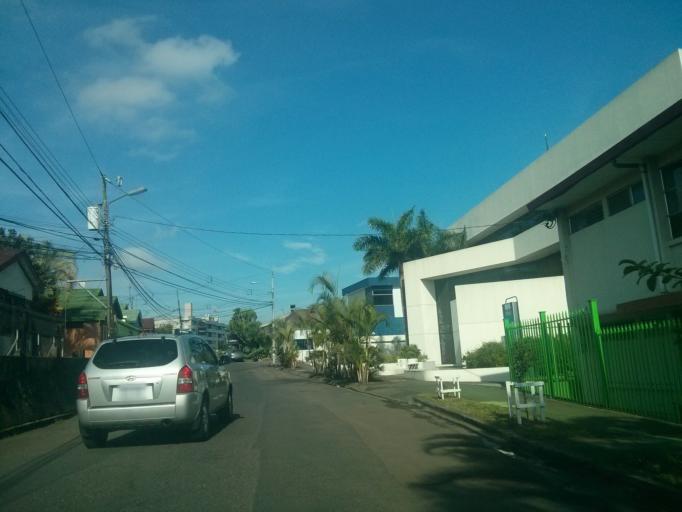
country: CR
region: San Jose
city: San Pedro
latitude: 9.9255
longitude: -84.0551
